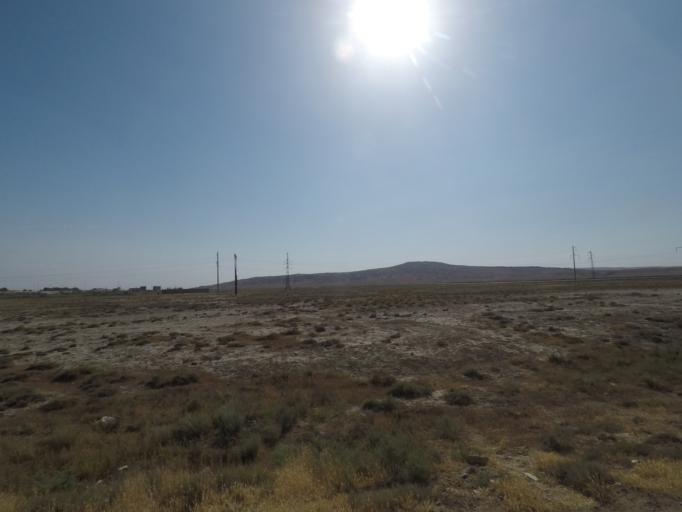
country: AZ
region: Baki
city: Qobustan
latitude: 39.9726
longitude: 49.3950
